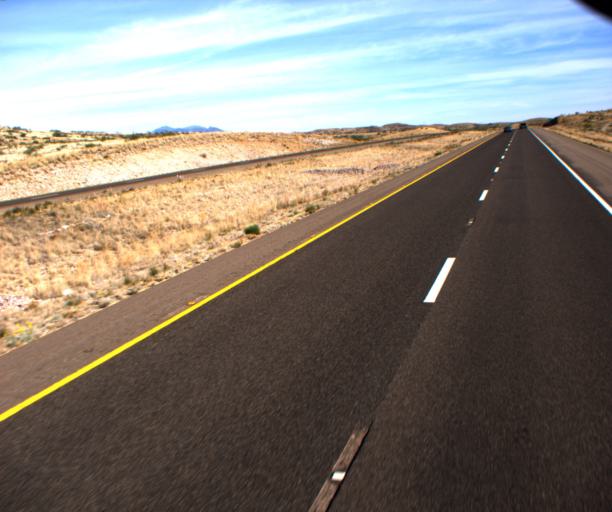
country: US
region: Arizona
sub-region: Cochise County
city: Willcox
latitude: 32.4247
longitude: -109.6627
